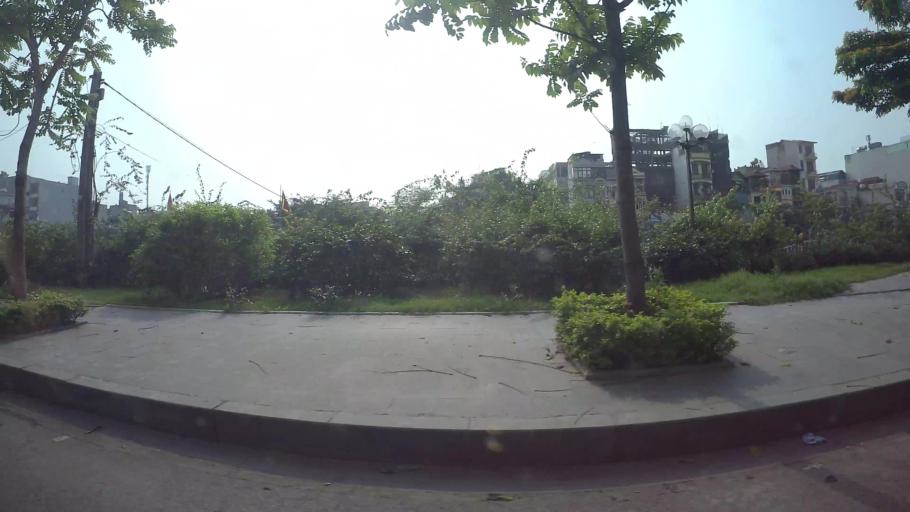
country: VN
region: Ha Noi
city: Thanh Xuan
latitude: 20.9904
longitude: 105.8138
